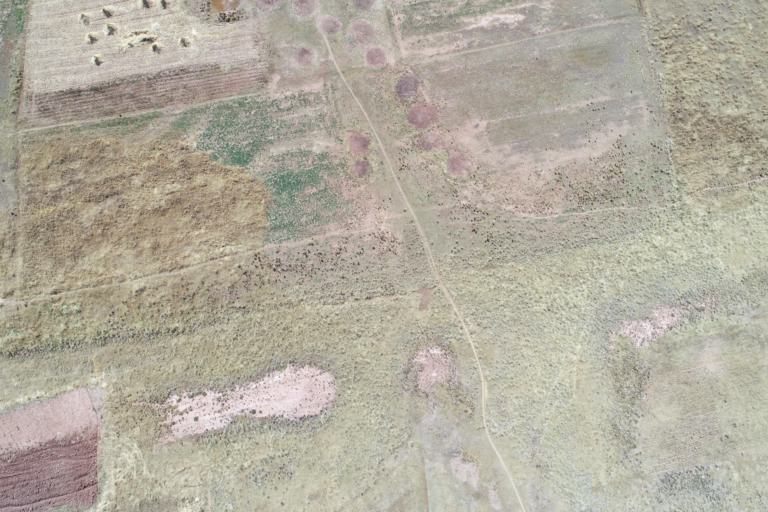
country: BO
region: La Paz
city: Tiahuanaco
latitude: -16.5931
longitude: -68.7706
